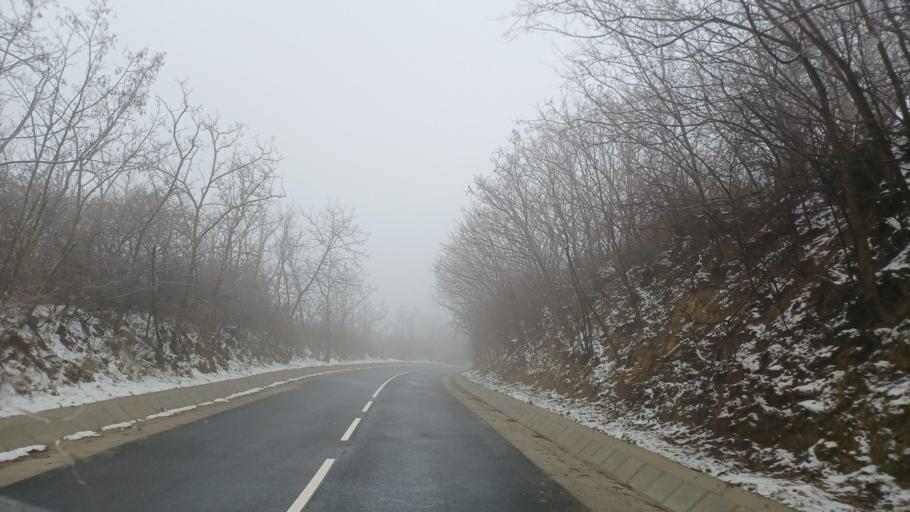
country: HU
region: Tolna
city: Gyonk
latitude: 46.5857
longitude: 18.4735
